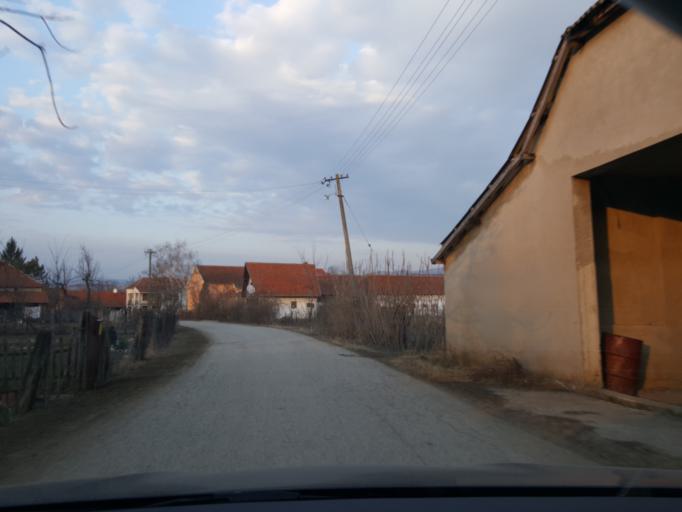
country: RS
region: Central Serbia
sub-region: Nisavski Okrug
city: Aleksinac
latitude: 43.5752
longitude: 21.6458
